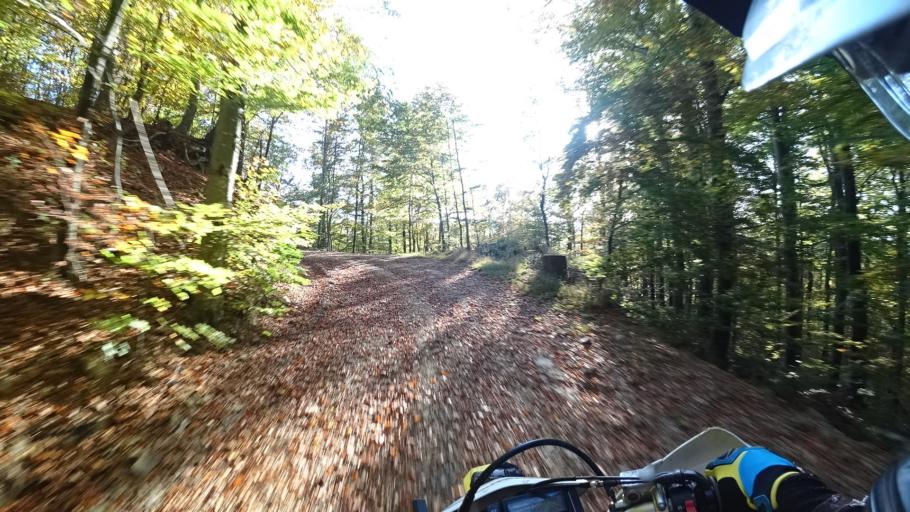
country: HR
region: Primorsko-Goranska
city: Klana
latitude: 45.4960
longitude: 14.3970
